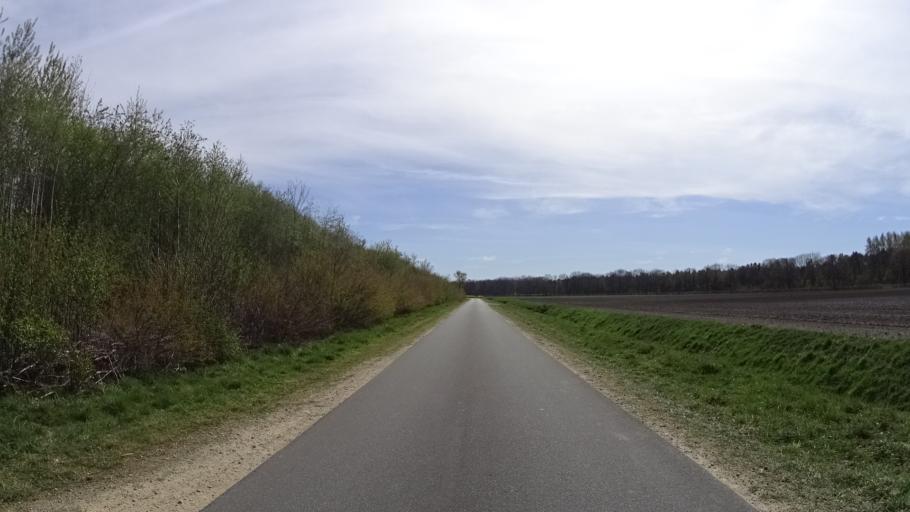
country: DE
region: Lower Saxony
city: Spelle
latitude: 52.3668
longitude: 7.4193
